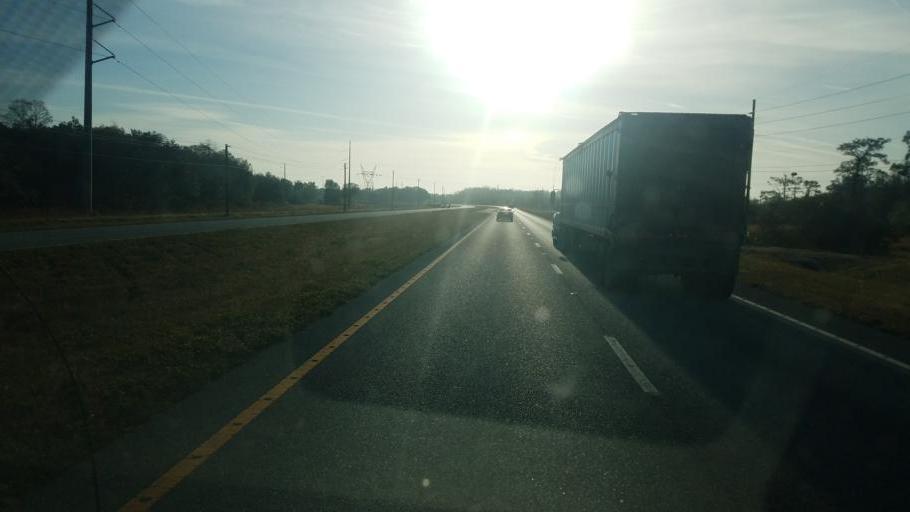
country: US
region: Florida
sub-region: Osceola County
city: Saint Cloud
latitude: 28.1474
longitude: -81.0951
